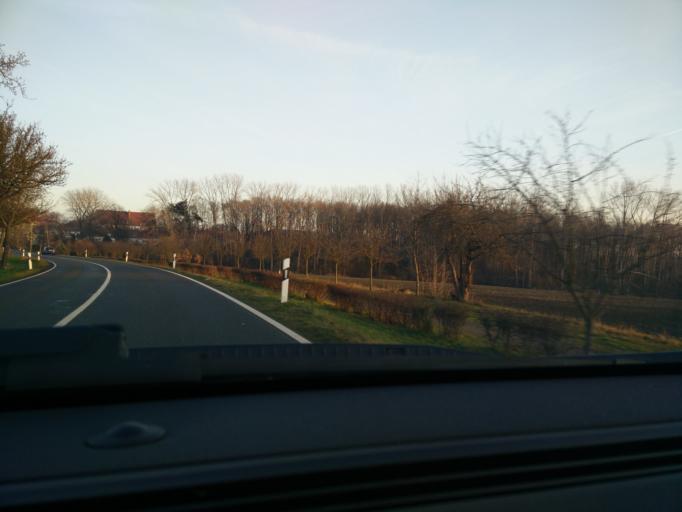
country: DE
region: Saxony
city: Kitzscher
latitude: 51.1642
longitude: 12.5441
